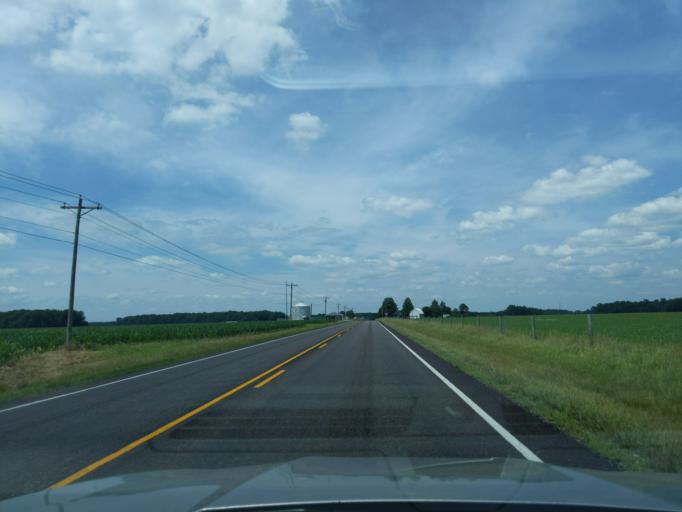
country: US
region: Indiana
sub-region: Ripley County
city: Osgood
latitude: 39.2320
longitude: -85.3395
